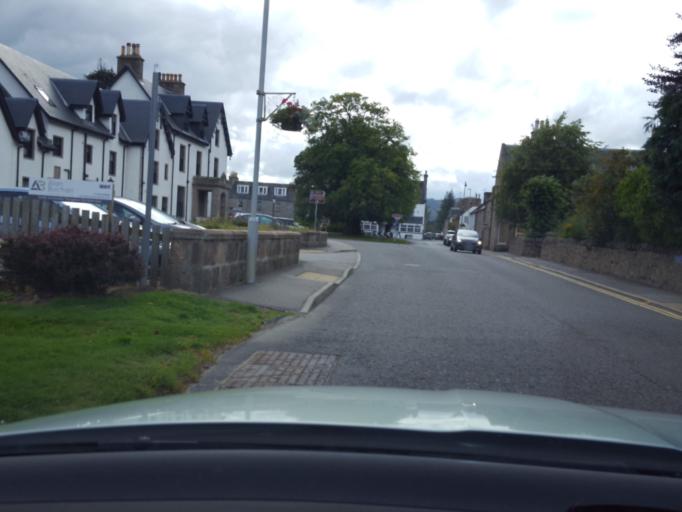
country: GB
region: Scotland
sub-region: Aberdeenshire
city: Ballater
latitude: 57.0483
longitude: -3.0366
